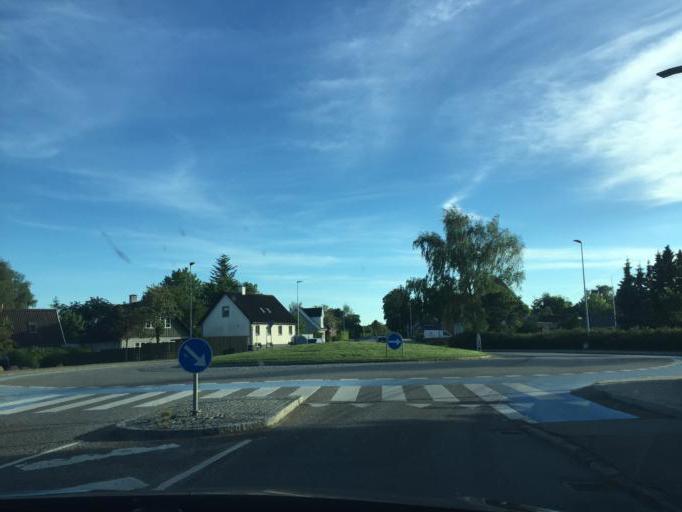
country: DK
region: Zealand
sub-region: Slagelse Kommune
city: Slagelse
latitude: 55.3929
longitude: 11.3320
